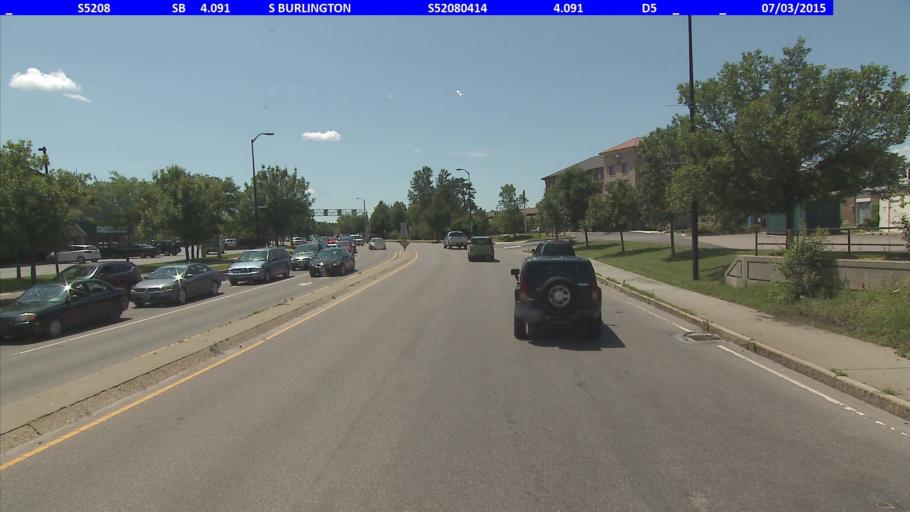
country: US
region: Vermont
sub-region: Chittenden County
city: South Burlington
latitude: 44.4689
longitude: -73.1814
